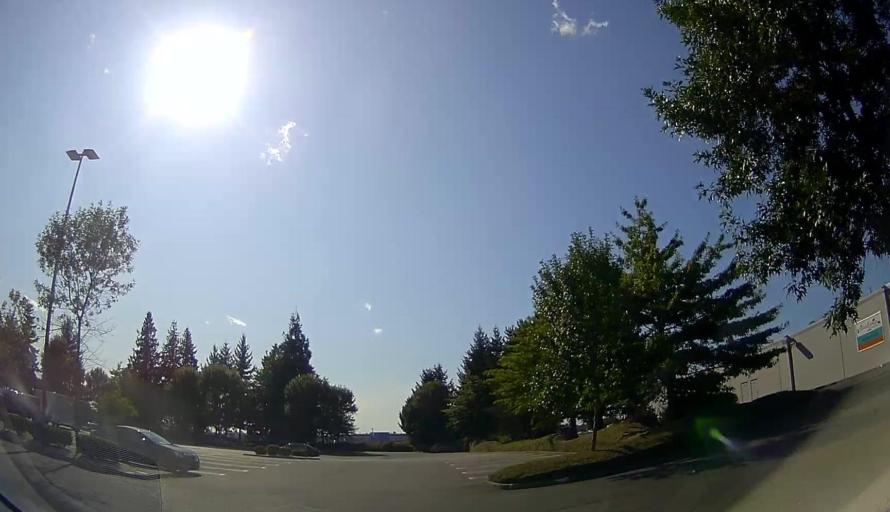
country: US
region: Washington
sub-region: Skagit County
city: Burlington
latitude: 48.4546
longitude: -122.3388
